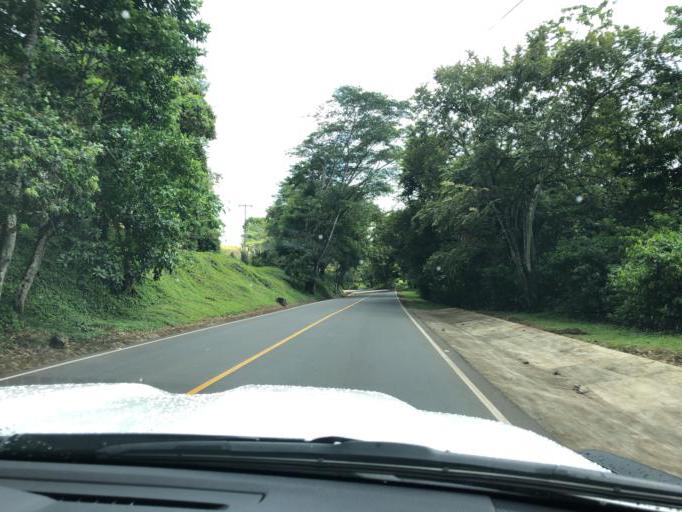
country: NI
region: Chontales
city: Villa Sandino
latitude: 11.9954
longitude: -84.9140
